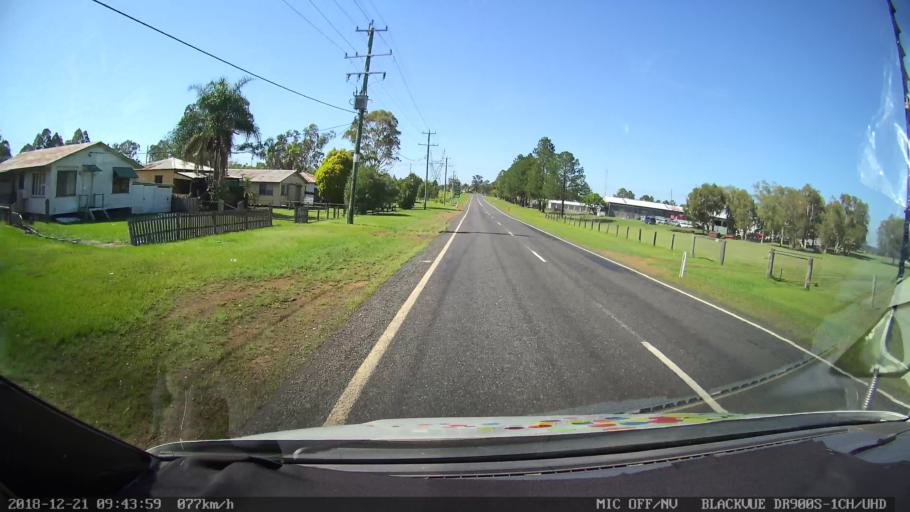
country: AU
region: New South Wales
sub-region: Clarence Valley
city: Grafton
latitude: -29.6129
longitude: 152.9347
